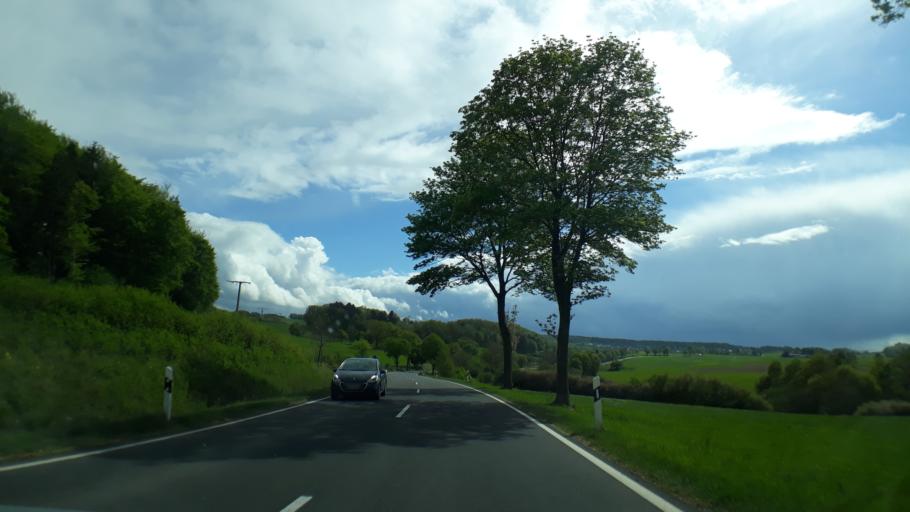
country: DE
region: North Rhine-Westphalia
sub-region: Regierungsbezirk Koln
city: Kall
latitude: 50.5075
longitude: 6.5375
